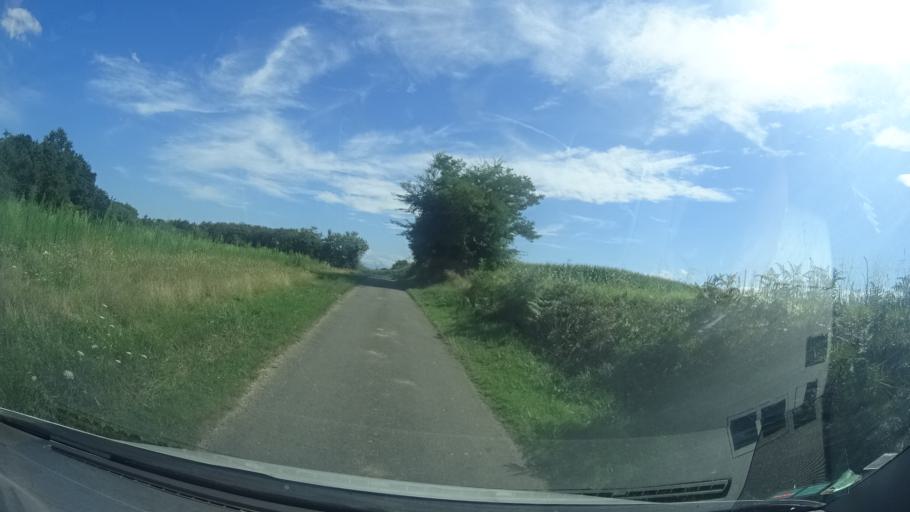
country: FR
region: Aquitaine
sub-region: Departement des Pyrenees-Atlantiques
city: Mont
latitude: 43.5004
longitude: -0.6760
